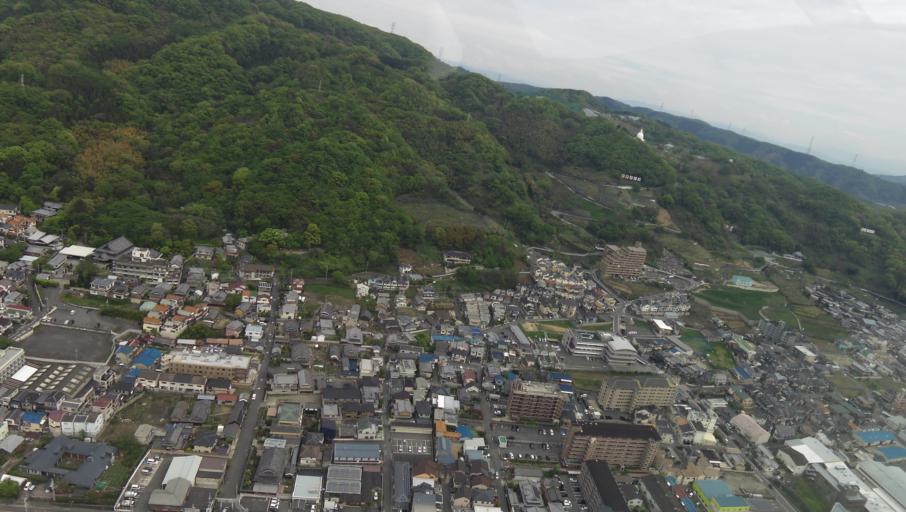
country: JP
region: Osaka
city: Kashihara
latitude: 34.5894
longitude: 135.6293
